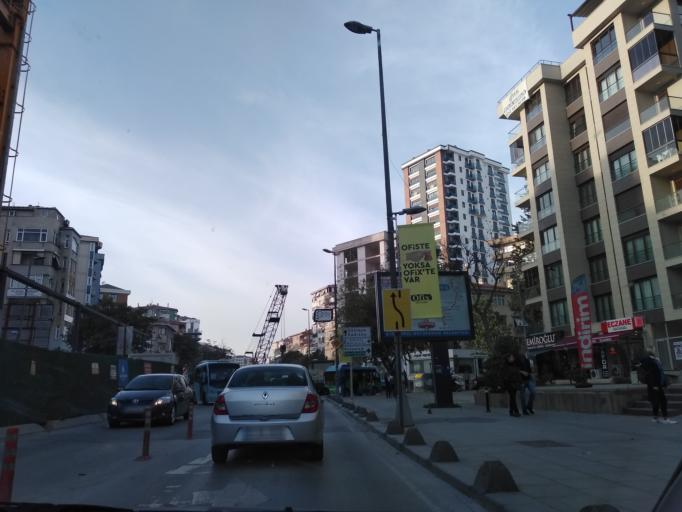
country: TR
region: Istanbul
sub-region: Atasehir
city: Atasehir
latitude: 40.9662
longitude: 29.0873
